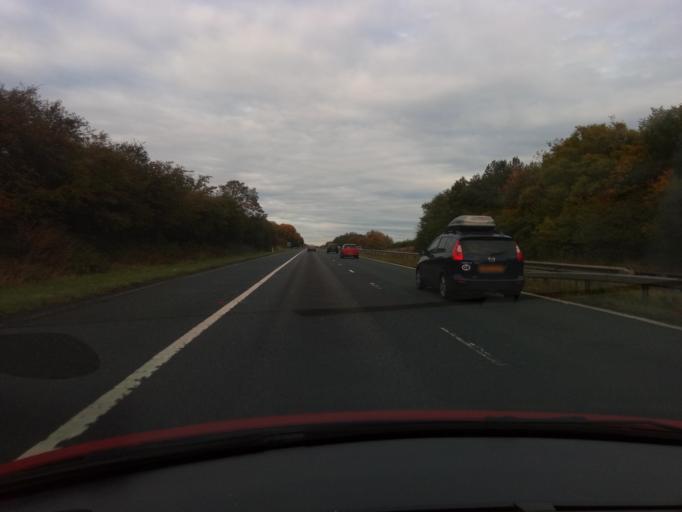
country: GB
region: England
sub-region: Darlington
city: High Coniscliffe
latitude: 54.5336
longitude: -1.6125
